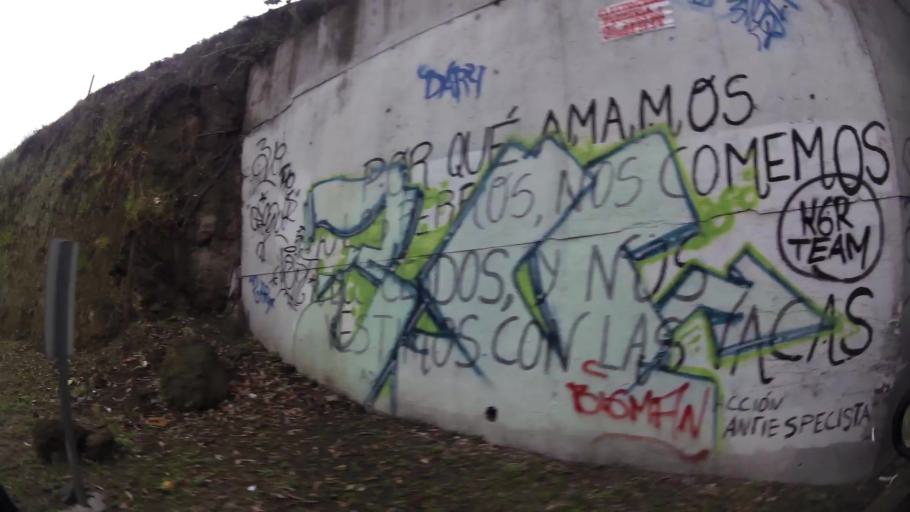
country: EC
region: Pichincha
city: Sangolqui
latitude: -0.2841
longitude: -78.4699
